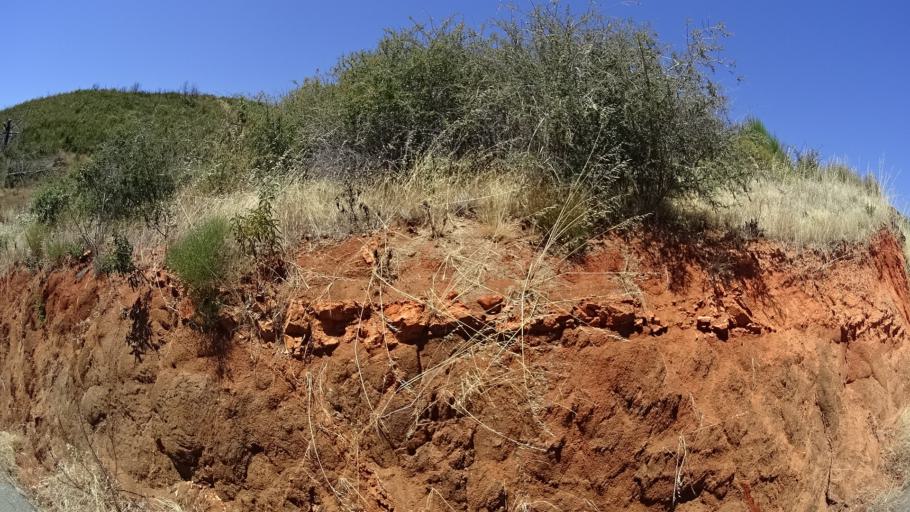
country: US
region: California
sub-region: Calaveras County
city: Mountain Ranch
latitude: 38.2894
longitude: -120.6226
